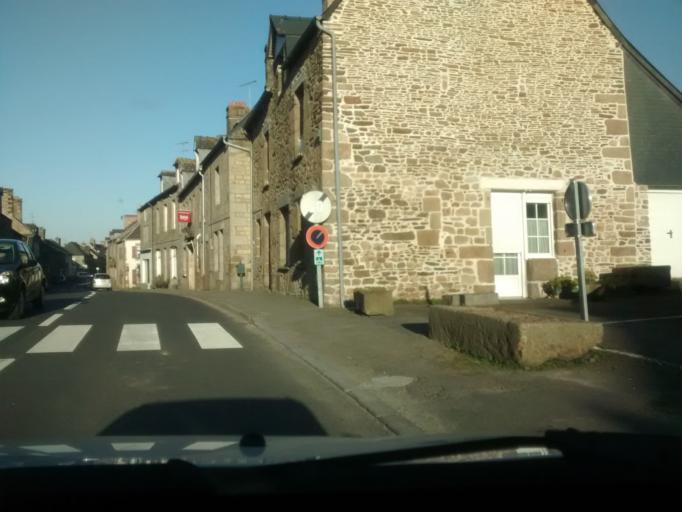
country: FR
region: Brittany
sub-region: Departement d'Ille-et-Vilaine
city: Pleine-Fougeres
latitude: 48.4964
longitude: -1.5876
